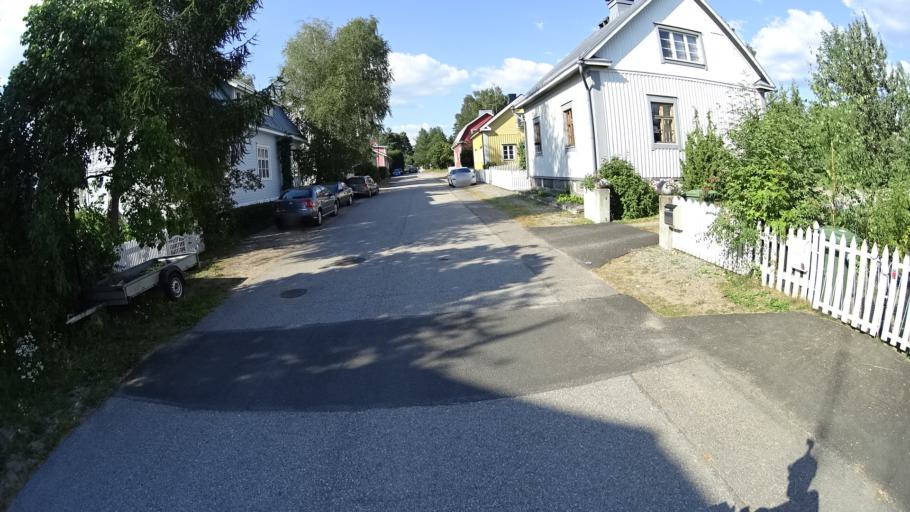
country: FI
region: Uusimaa
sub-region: Porvoo
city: Porvoo
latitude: 60.3993
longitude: 25.6733
